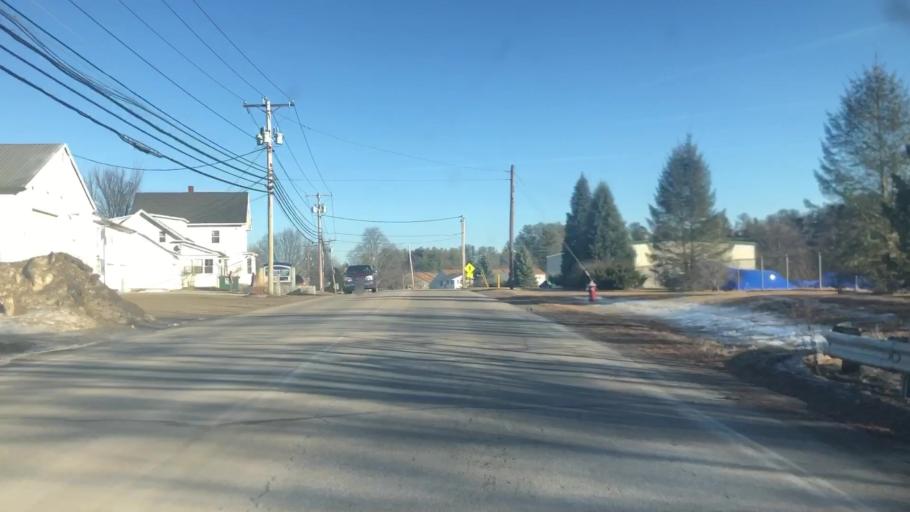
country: US
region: New Hampshire
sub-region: Hillsborough County
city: Milford
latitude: 42.8411
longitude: -71.6825
